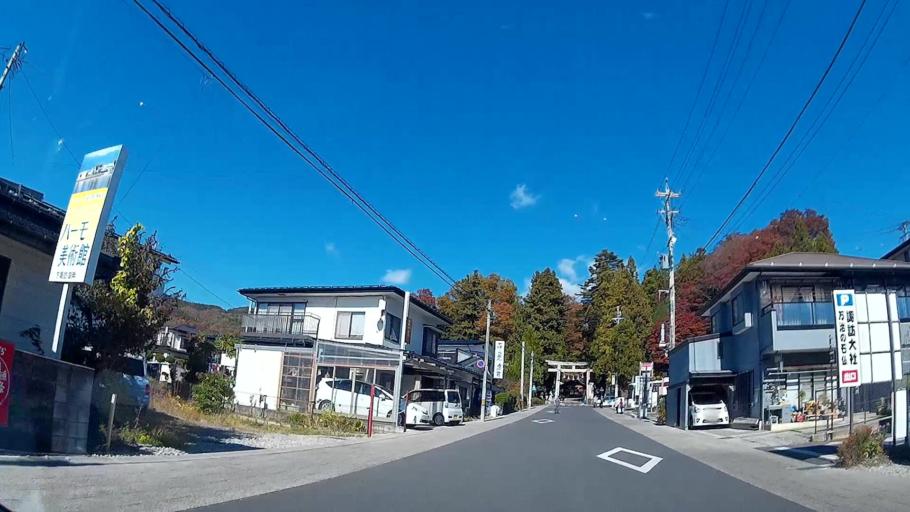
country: JP
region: Nagano
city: Okaya
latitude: 36.0804
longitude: 138.0819
